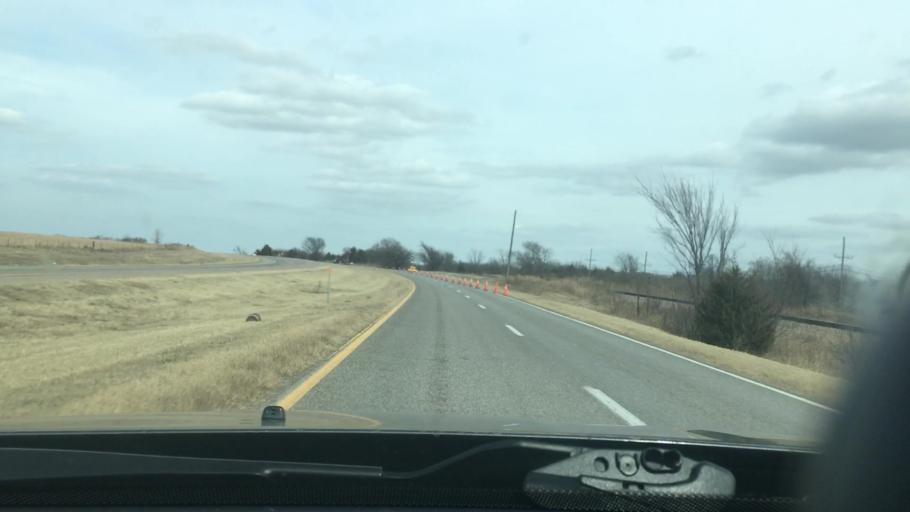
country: US
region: Oklahoma
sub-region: Pontotoc County
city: Ada
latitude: 34.7022
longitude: -96.7330
